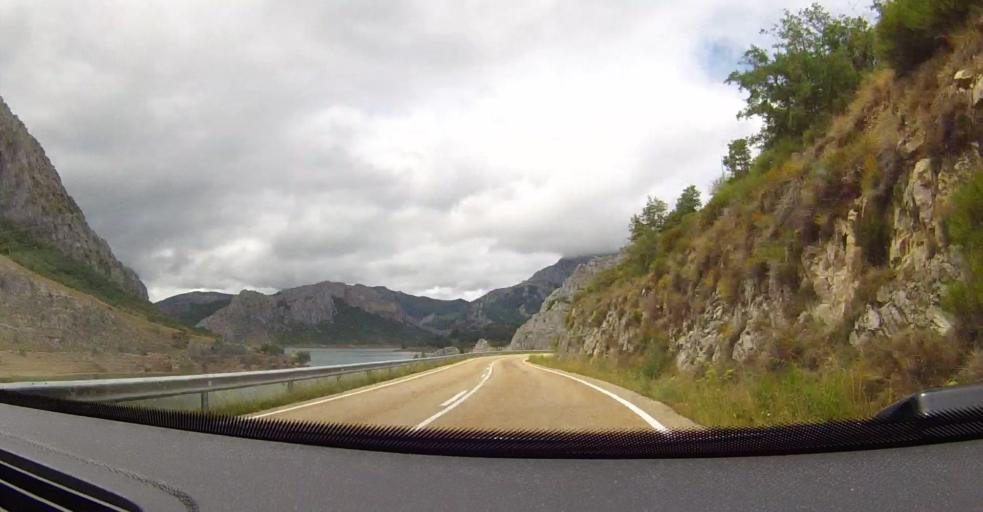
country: ES
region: Castille and Leon
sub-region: Provincia de Leon
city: Reyero
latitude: 42.9574
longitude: -5.2507
